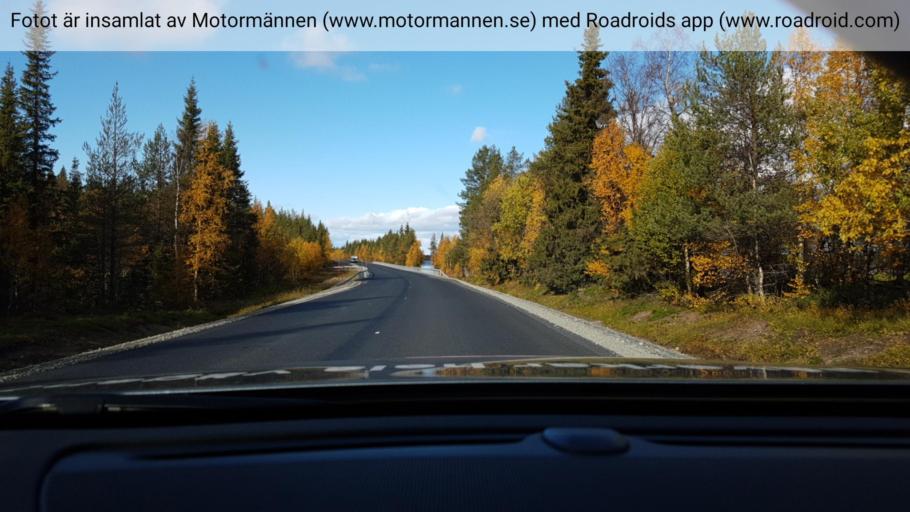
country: SE
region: Norrbotten
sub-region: Arjeplogs Kommun
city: Arjeplog
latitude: 65.9680
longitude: 18.2632
